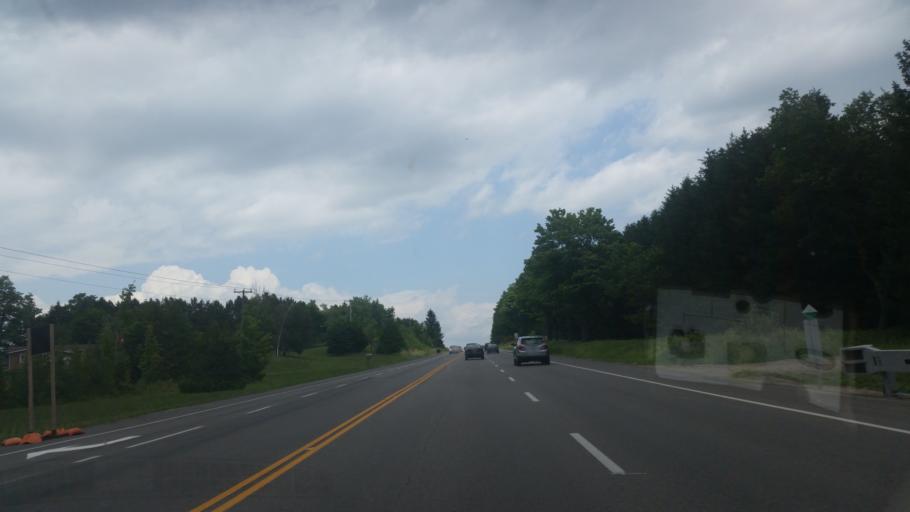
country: CA
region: Ontario
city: Orangeville
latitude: 43.7087
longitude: -80.1222
